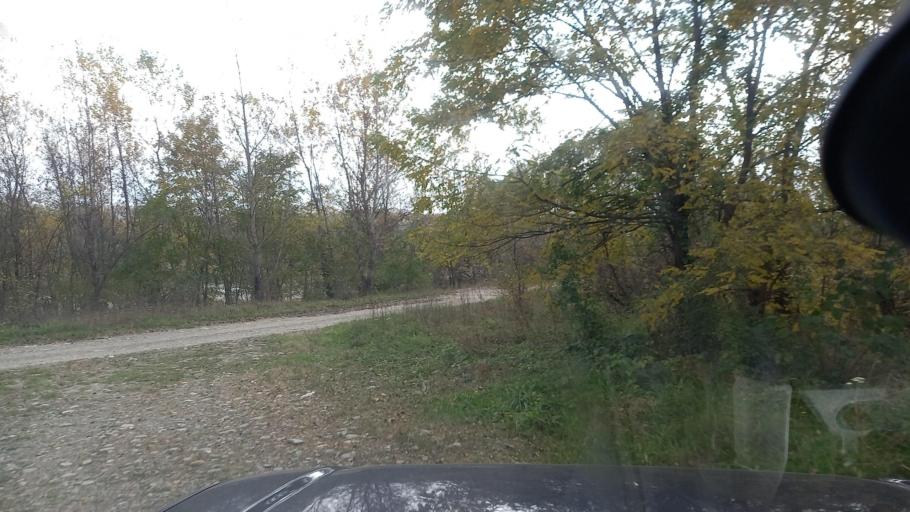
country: RU
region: Krasnodarskiy
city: Shedok
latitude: 44.1763
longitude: 40.8504
